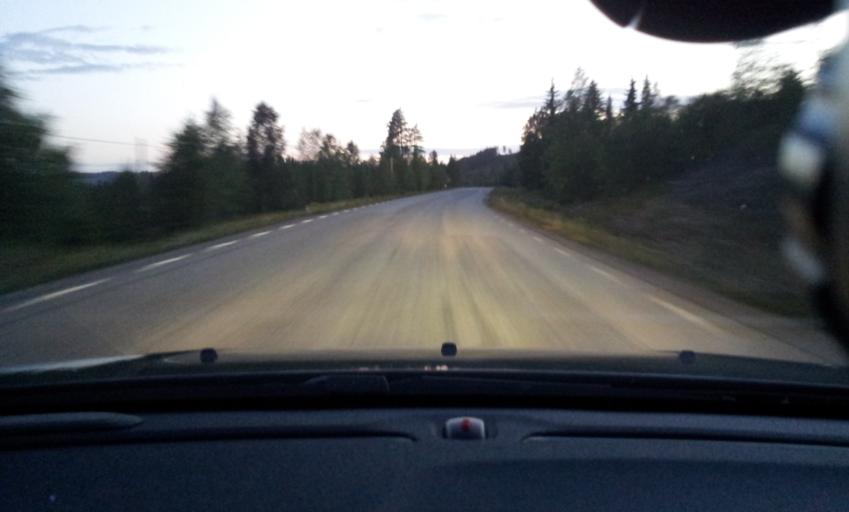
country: SE
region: Jaemtland
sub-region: Braecke Kommun
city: Braecke
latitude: 62.7570
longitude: 15.0493
